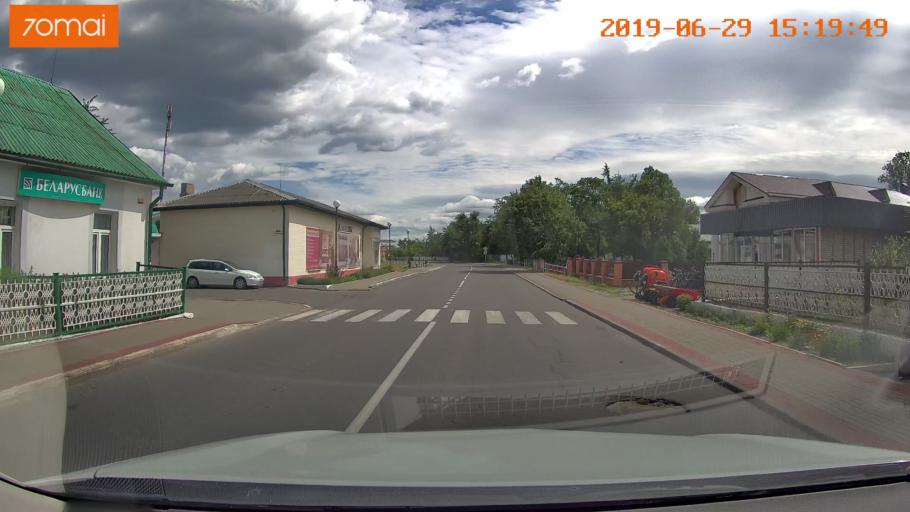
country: BY
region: Brest
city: Mikashevichy
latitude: 52.2177
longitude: 27.4703
